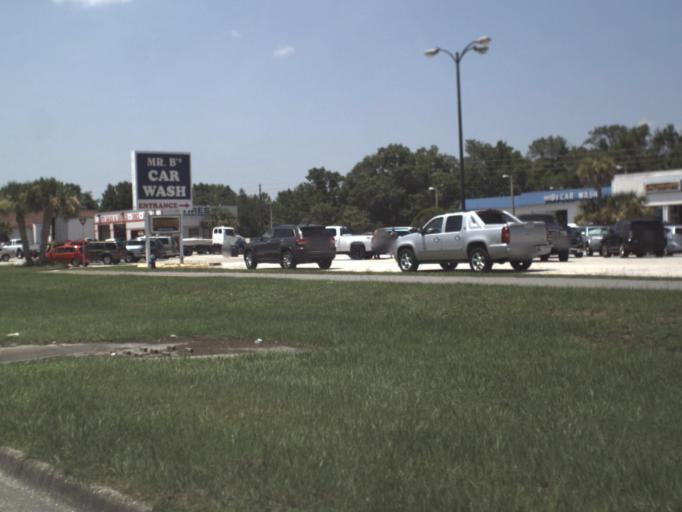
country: US
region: Florida
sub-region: Citrus County
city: Crystal River
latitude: 28.8899
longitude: -82.5847
